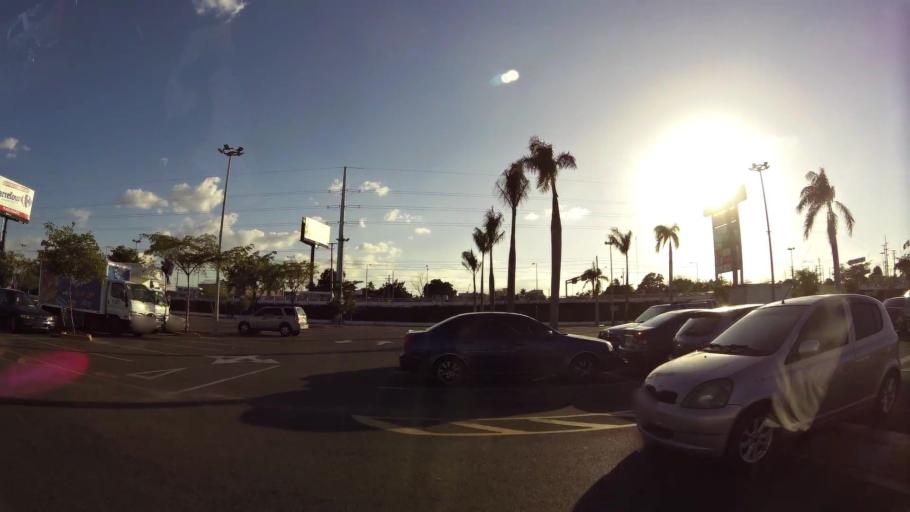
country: DO
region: Nacional
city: Santo Domingo
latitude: 18.4880
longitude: -69.9784
